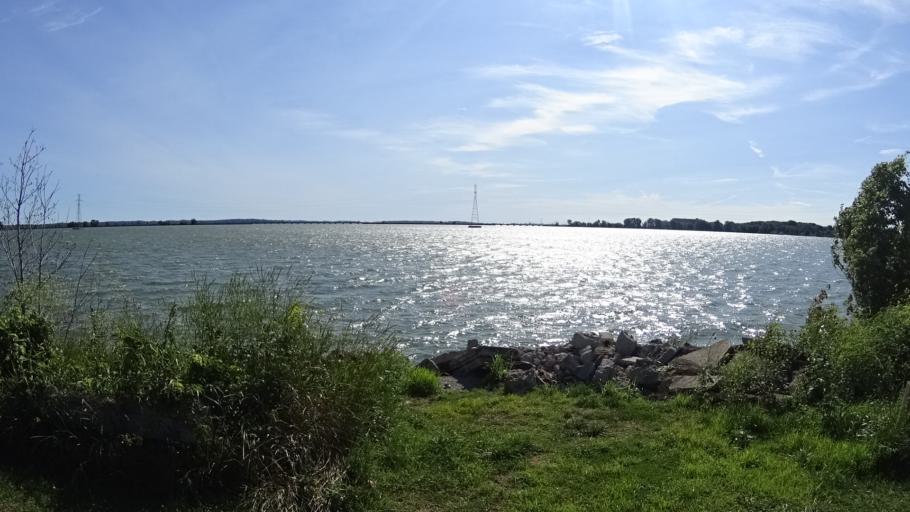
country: US
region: Ohio
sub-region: Ottawa County
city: Port Clinton
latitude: 41.4747
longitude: -82.8263
